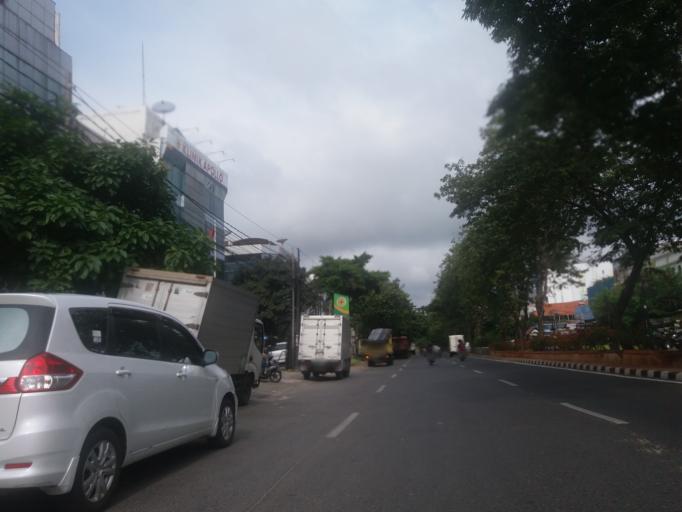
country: ID
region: Jakarta Raya
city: Jakarta
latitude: -6.1413
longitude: 106.8273
